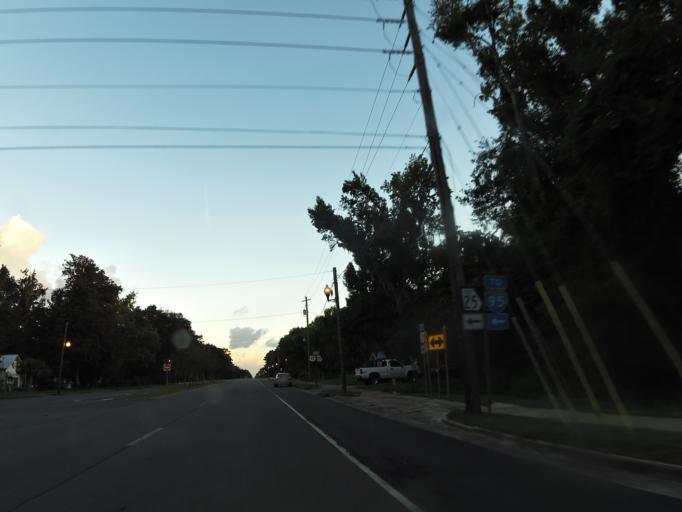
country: US
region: Georgia
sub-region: Camden County
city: Woodbine
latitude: 30.9602
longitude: -81.7222
